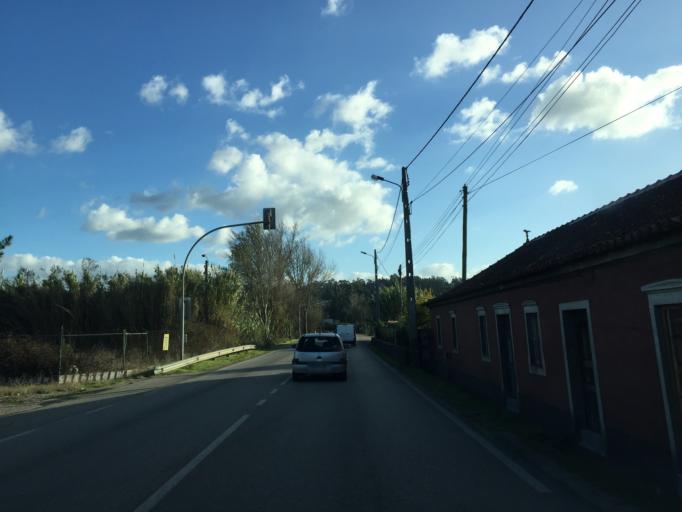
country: PT
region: Leiria
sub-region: Leiria
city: Souto da Carpalhosa
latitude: 39.8651
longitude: -8.8391
